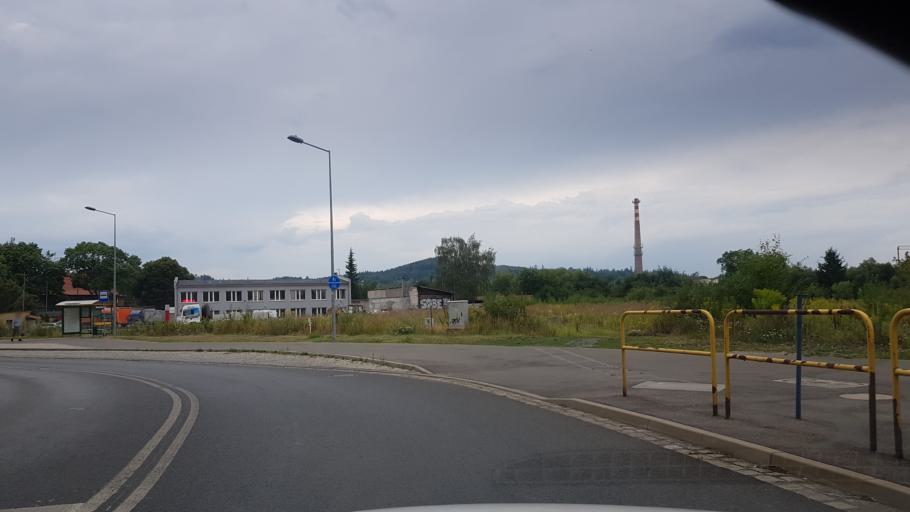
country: PL
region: Lower Silesian Voivodeship
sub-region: Jelenia Gora
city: Jelenia Gora
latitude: 50.9068
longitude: 15.7448
